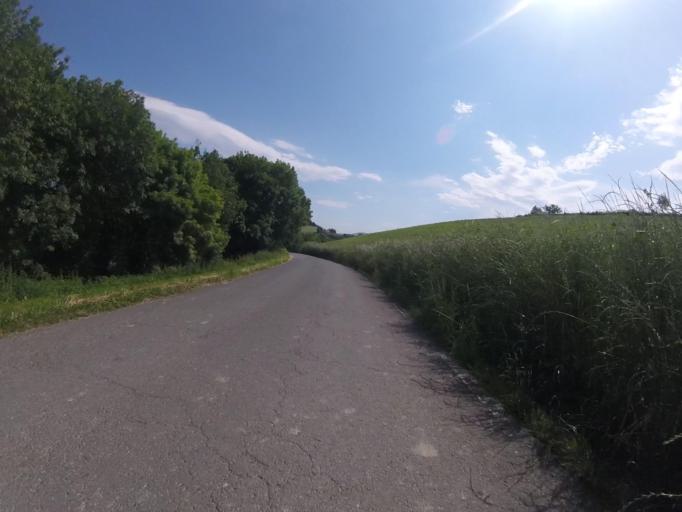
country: ES
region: Basque Country
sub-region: Provincia de Guipuzcoa
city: Orendain
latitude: 43.0799
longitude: -2.1105
